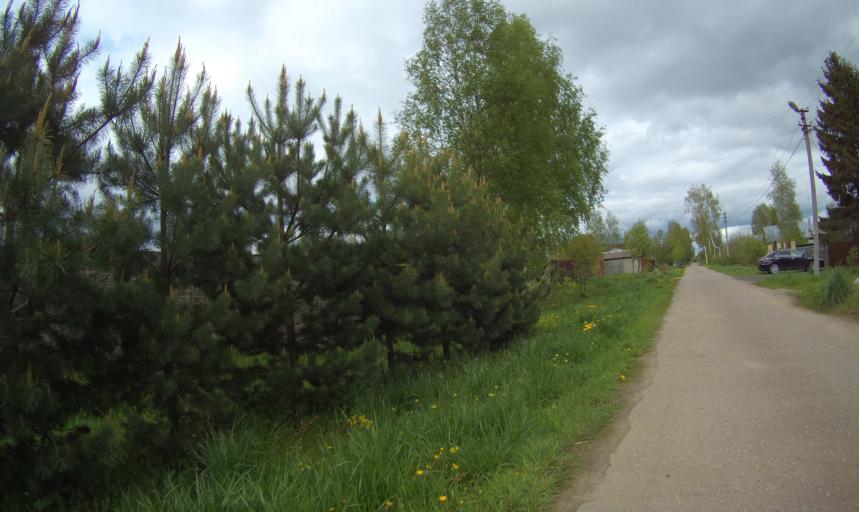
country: RU
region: Moskovskaya
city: Rechitsy
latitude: 55.5712
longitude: 38.4863
